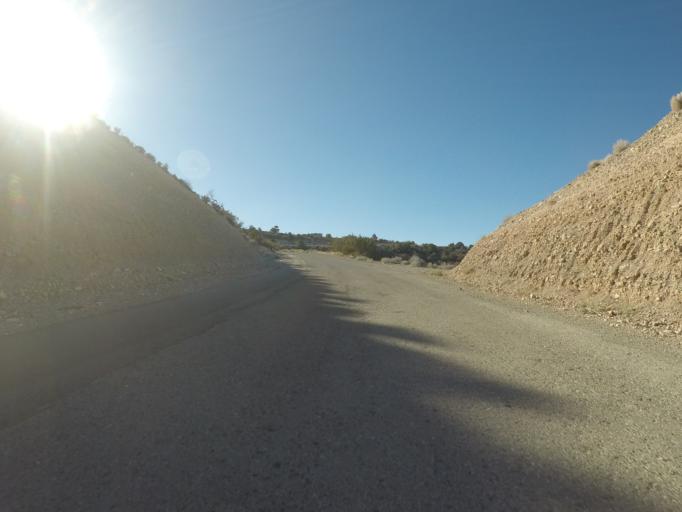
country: US
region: Nevada
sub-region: Clark County
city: Summerlin South
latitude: 36.0838
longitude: -115.5597
